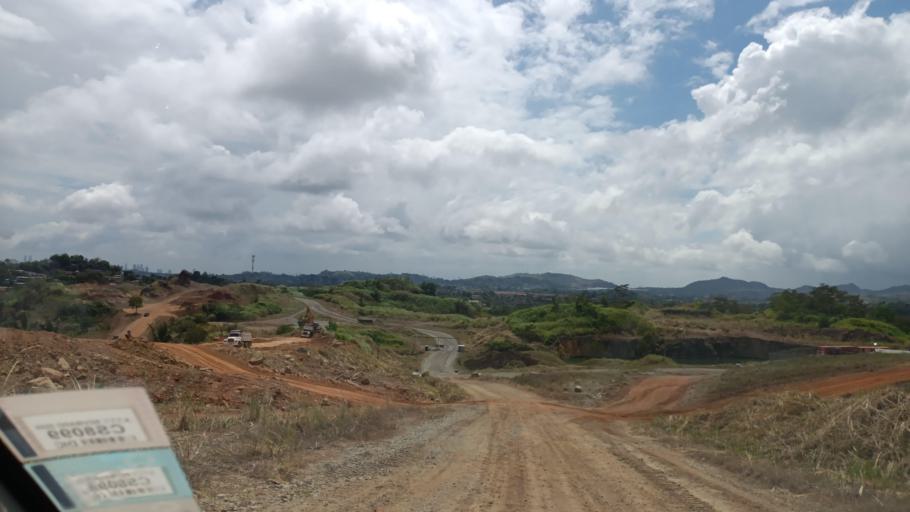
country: PA
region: Panama
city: Las Cumbres
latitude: 9.1097
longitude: -79.4994
